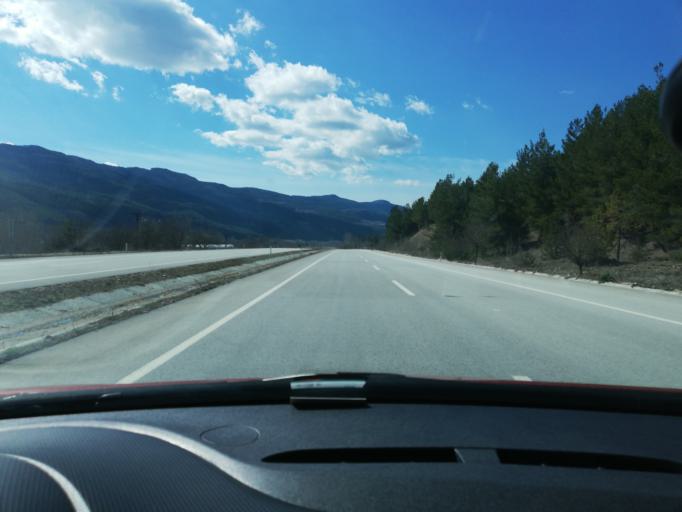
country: TR
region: Karabuk
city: Ovacik
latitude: 41.2038
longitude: 32.8607
